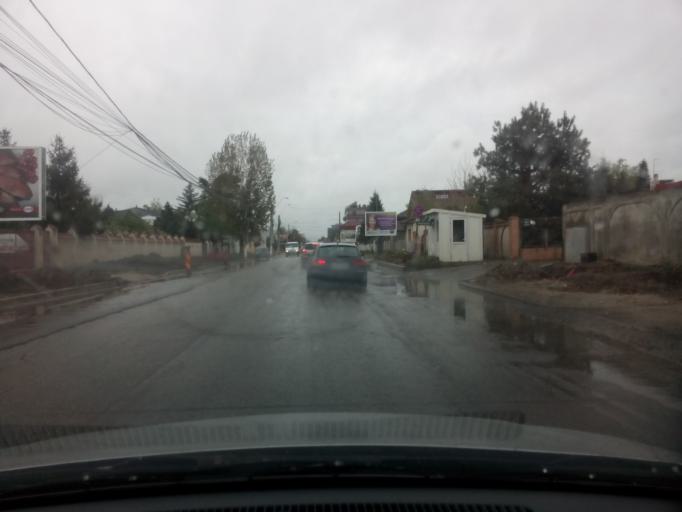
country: RO
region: Ilfov
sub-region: Comuna Tunari
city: Tunari
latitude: 44.5141
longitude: 26.1284
